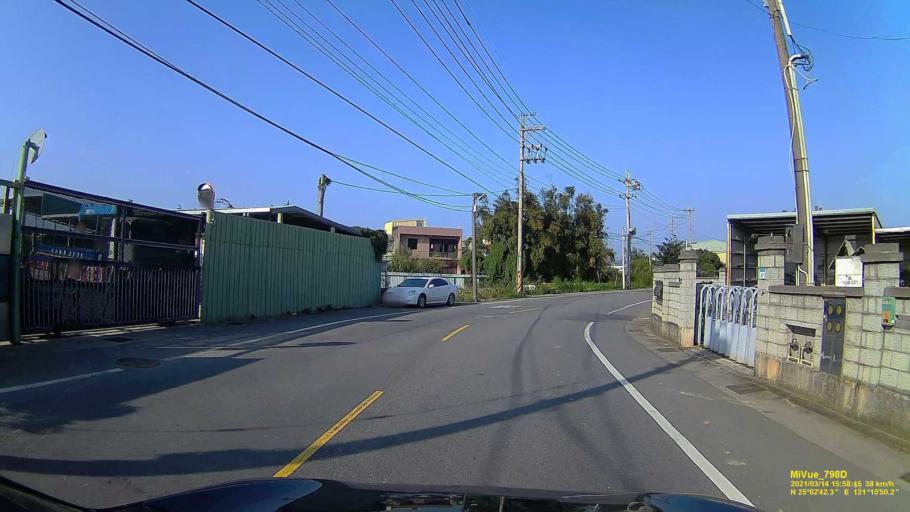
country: TW
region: Taiwan
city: Taoyuan City
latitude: 25.0452
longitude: 121.2642
